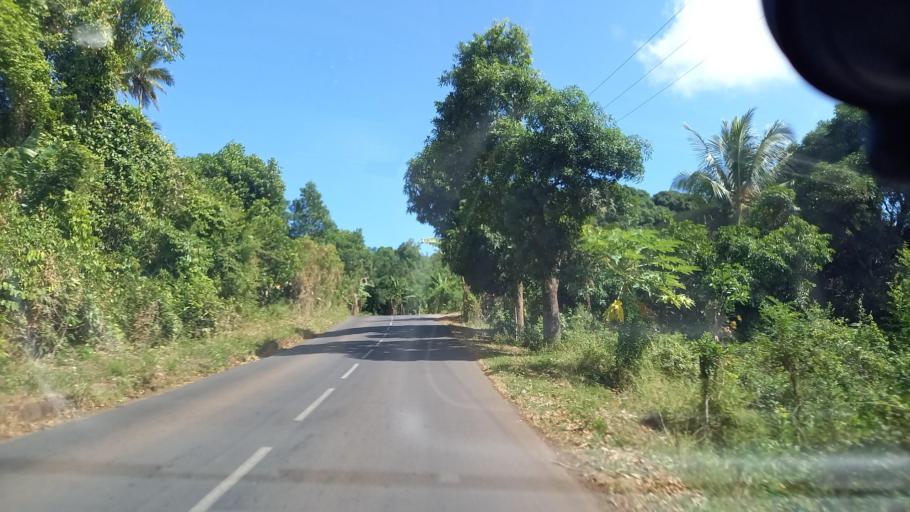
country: YT
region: Mamoudzou
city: Mamoudzou
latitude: -12.7934
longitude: 45.1897
